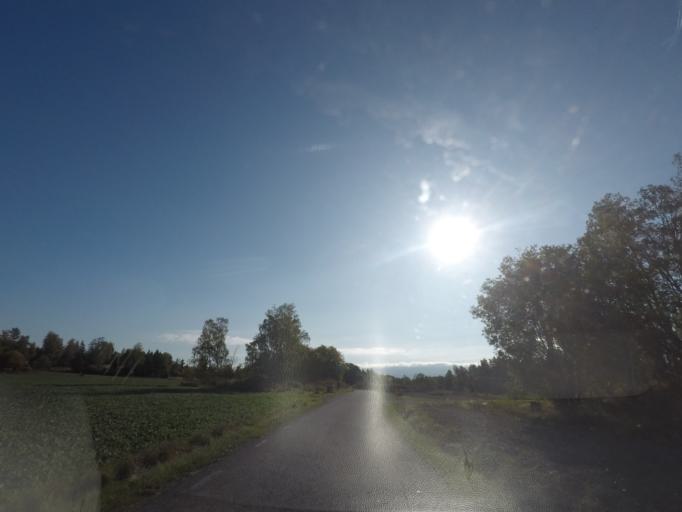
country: SE
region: Soedermanland
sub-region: Eskilstuna Kommun
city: Kvicksund
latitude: 59.5429
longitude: 16.3653
